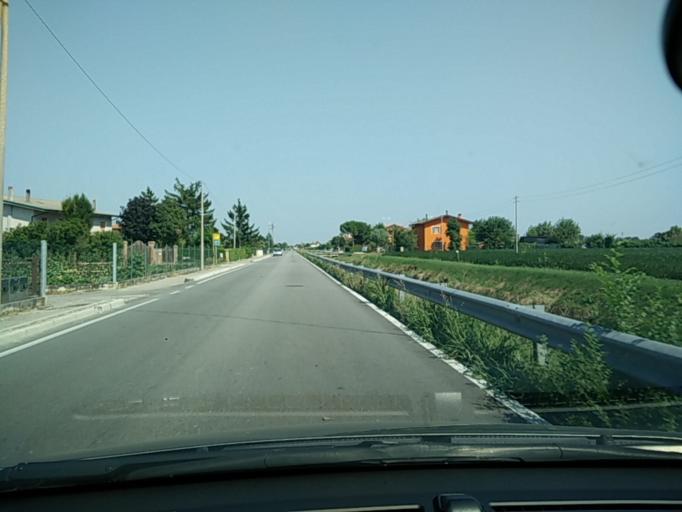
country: IT
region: Veneto
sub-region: Provincia di Venezia
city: Passarella
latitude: 45.6212
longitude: 12.6076
